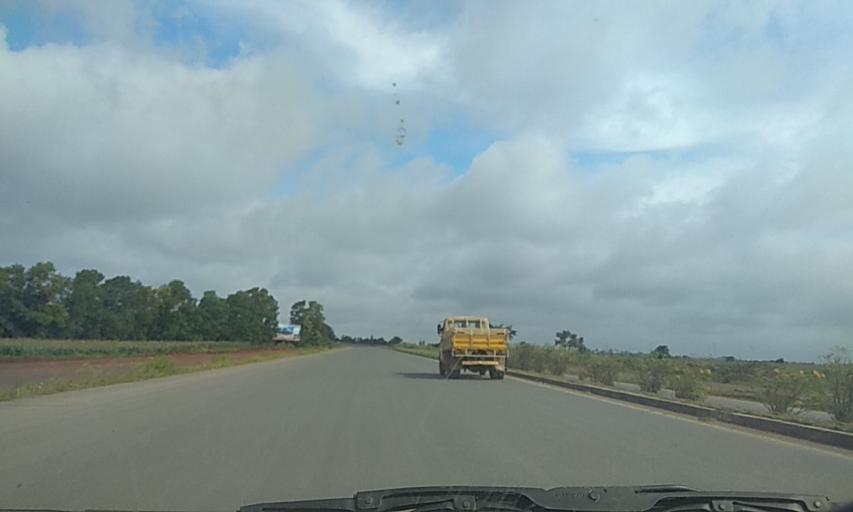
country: IN
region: Karnataka
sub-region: Haveri
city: Shiggaon
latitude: 15.0511
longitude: 75.1680
